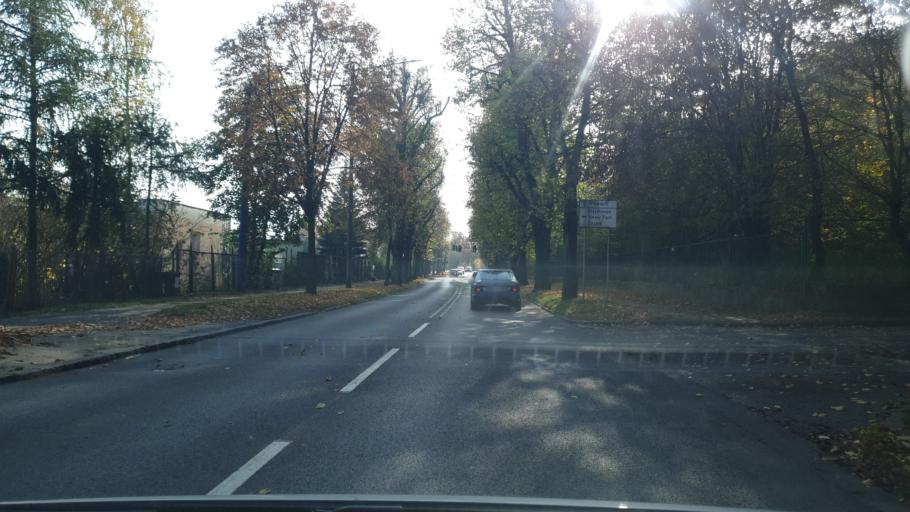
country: PL
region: Pomeranian Voivodeship
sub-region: Sopot
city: Sopot
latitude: 54.3996
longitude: 18.5629
